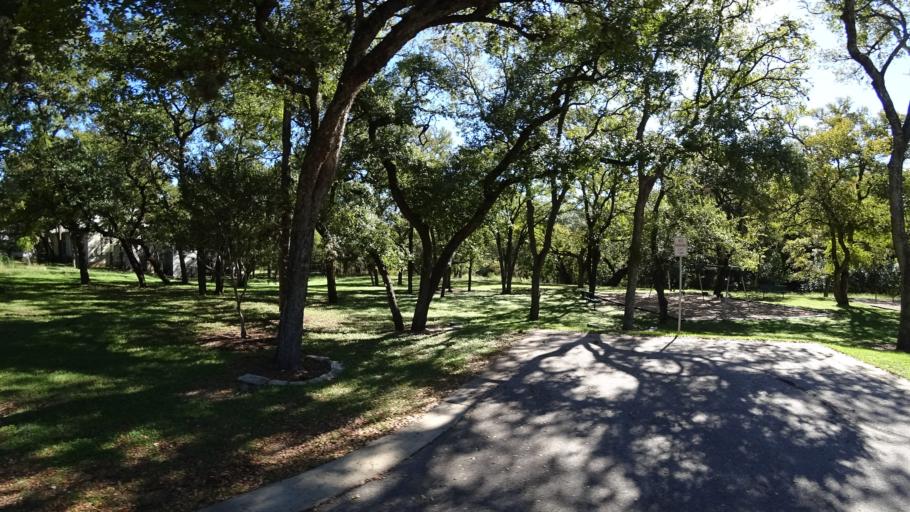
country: US
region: Texas
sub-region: Travis County
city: Rollingwood
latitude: 30.2209
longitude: -97.8101
